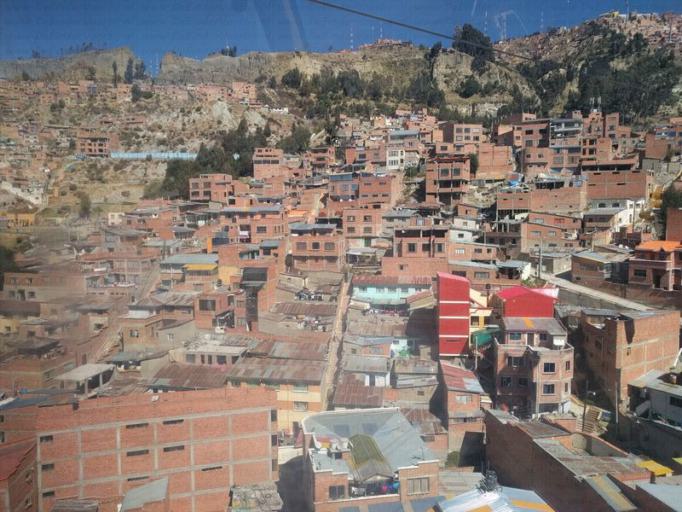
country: BO
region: La Paz
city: La Paz
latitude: -16.5151
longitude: -68.1405
